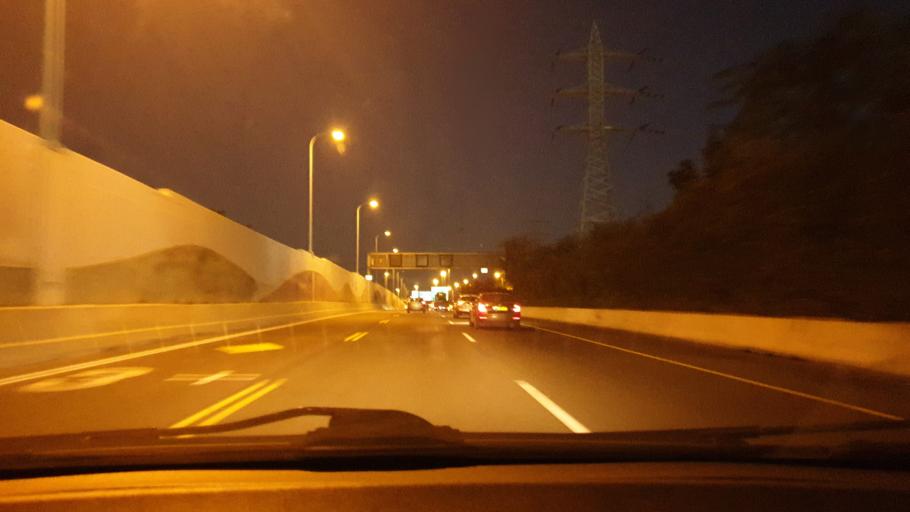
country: IL
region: Tel Aviv
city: Yafo
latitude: 32.0377
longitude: 34.7656
